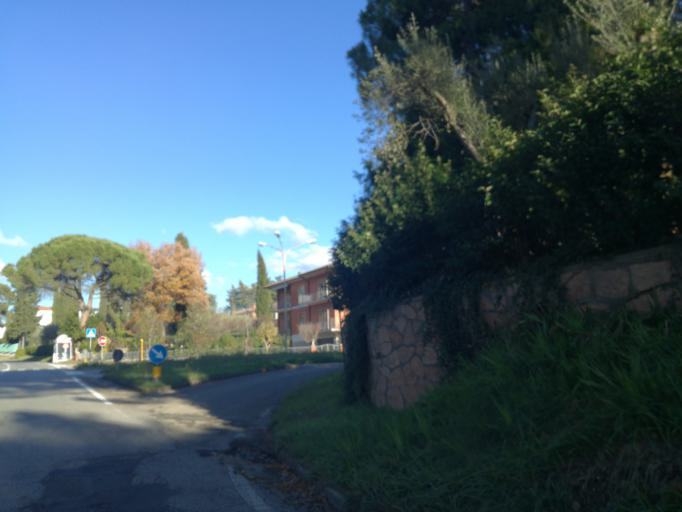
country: IT
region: Umbria
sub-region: Provincia di Perugia
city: Perugia
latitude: 43.0776
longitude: 12.3988
